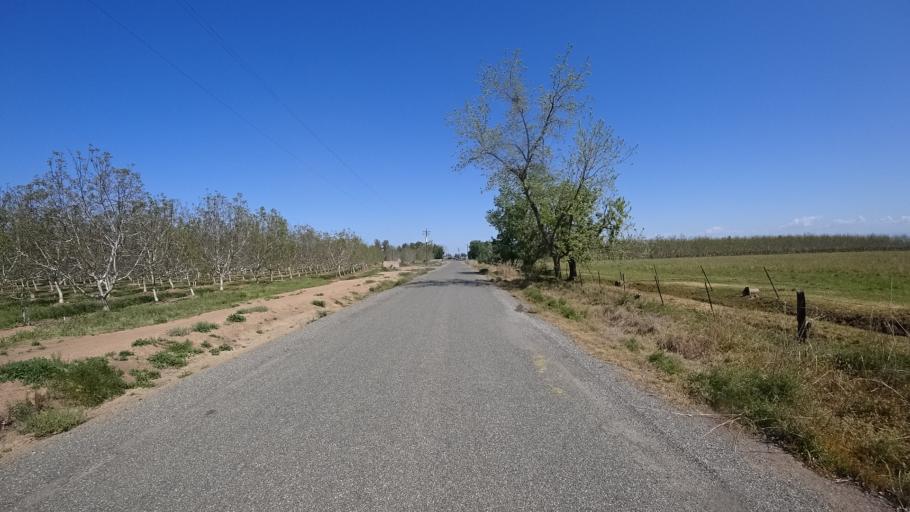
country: US
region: California
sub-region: Glenn County
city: Orland
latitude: 39.7932
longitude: -122.1598
